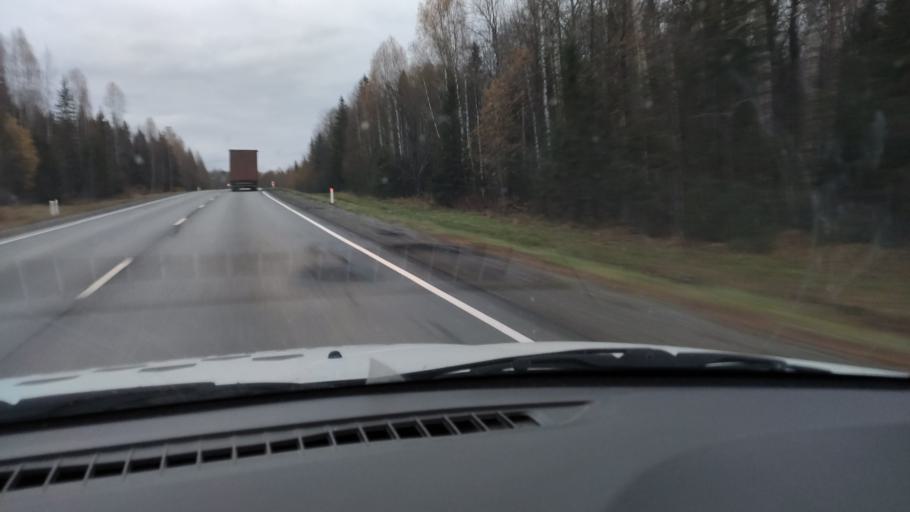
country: RU
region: Kirov
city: Kostino
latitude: 58.8008
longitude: 52.9049
